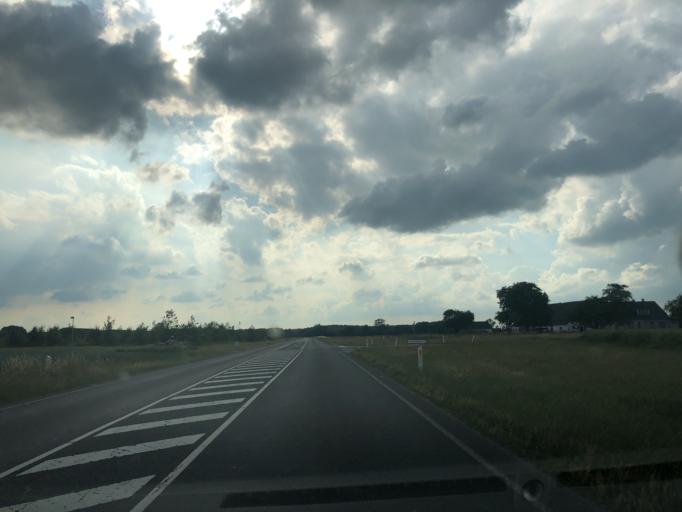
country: DK
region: Zealand
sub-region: Stevns Kommune
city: Harlev
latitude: 55.3154
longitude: 12.2048
